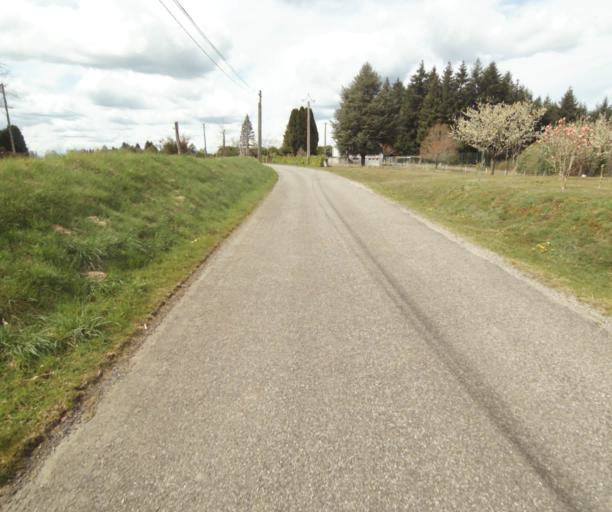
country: FR
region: Limousin
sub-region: Departement de la Correze
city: Laguenne
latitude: 45.2287
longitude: 1.8775
